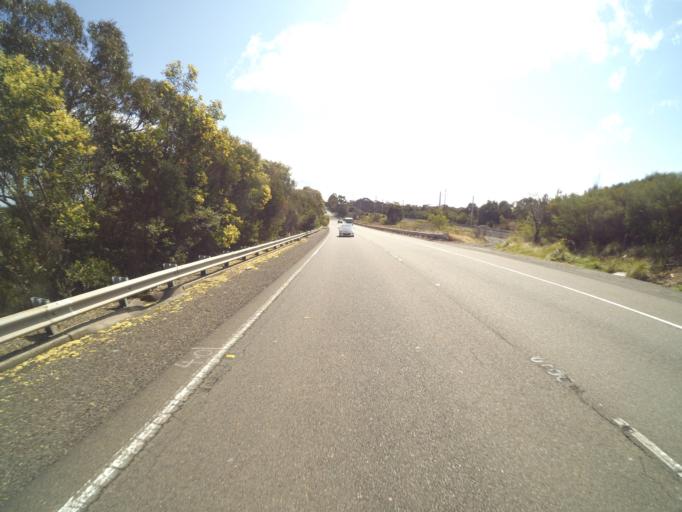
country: AU
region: New South Wales
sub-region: Sutherland Shire
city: Heathcote
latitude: -34.1106
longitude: 150.9934
